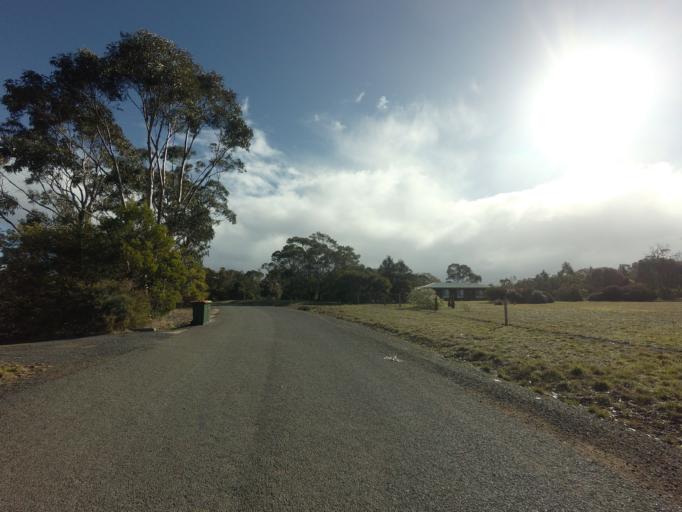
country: AU
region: Tasmania
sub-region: Sorell
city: Sorell
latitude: -42.3069
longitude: 147.9958
